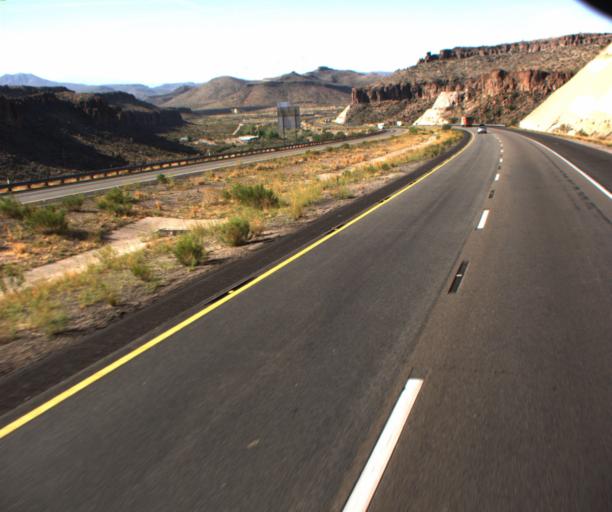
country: US
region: Arizona
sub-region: Mohave County
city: Kingman
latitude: 35.1755
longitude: -114.0751
